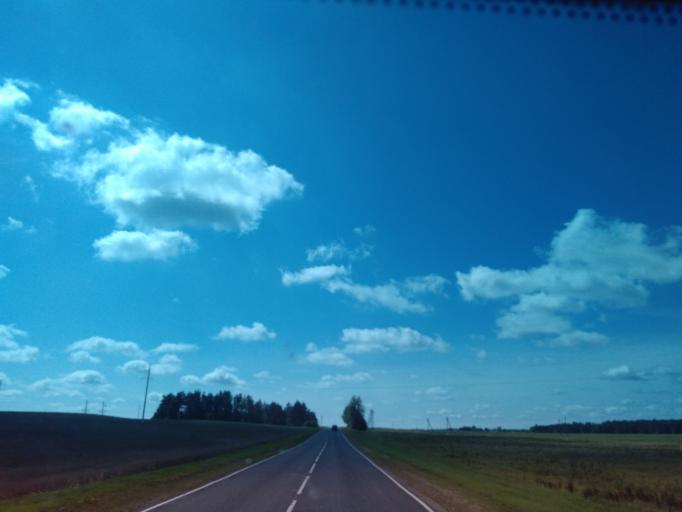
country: BY
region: Minsk
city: Uzda
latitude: 53.3852
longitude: 27.2424
